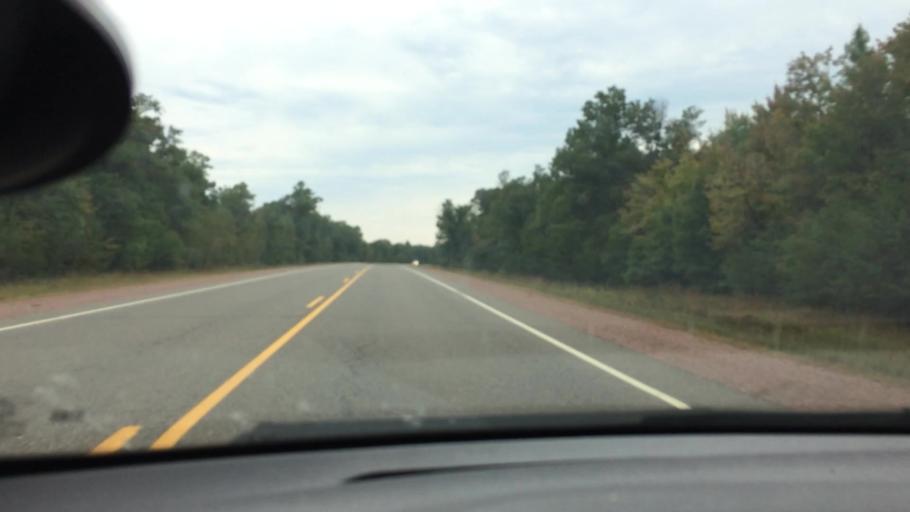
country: US
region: Wisconsin
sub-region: Clark County
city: Neillsville
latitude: 44.5665
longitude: -90.7162
